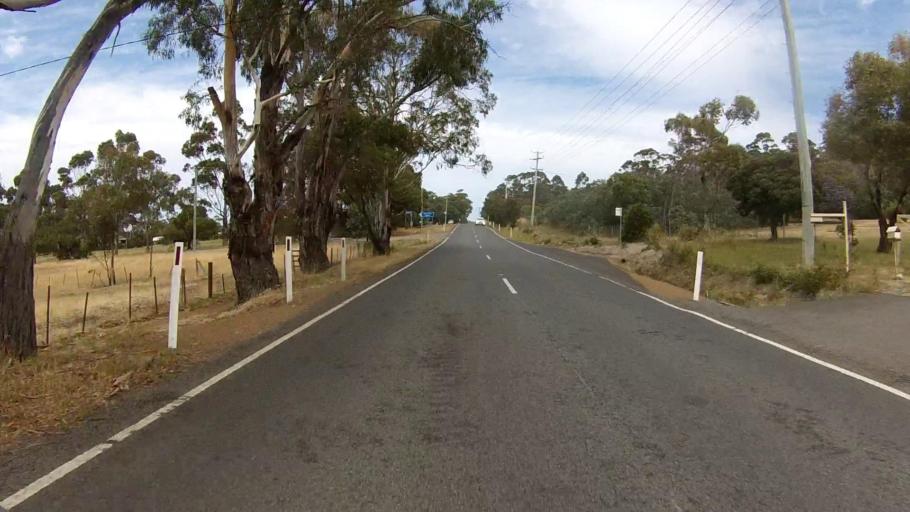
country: AU
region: Tasmania
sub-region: Clarence
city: Acton Park
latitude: -42.8950
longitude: 147.4813
